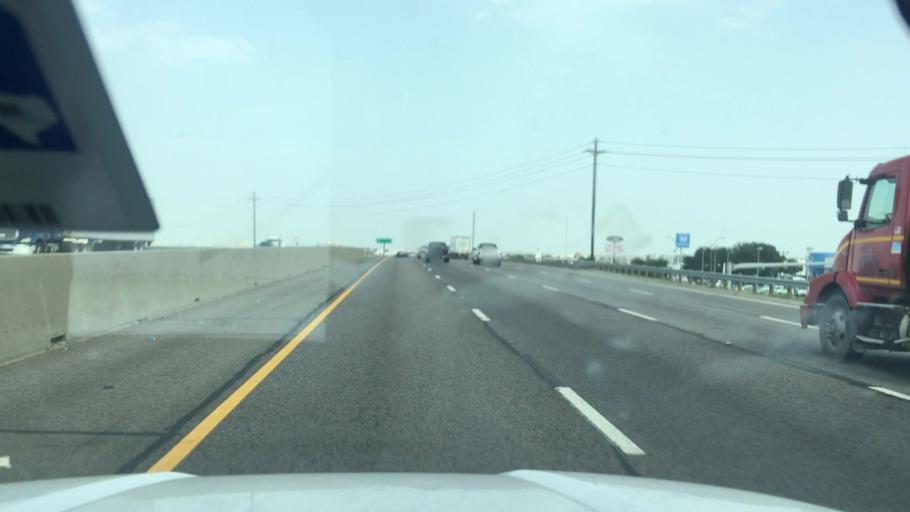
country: US
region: Texas
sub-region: Dallas County
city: Duncanville
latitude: 32.6483
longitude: -96.8644
